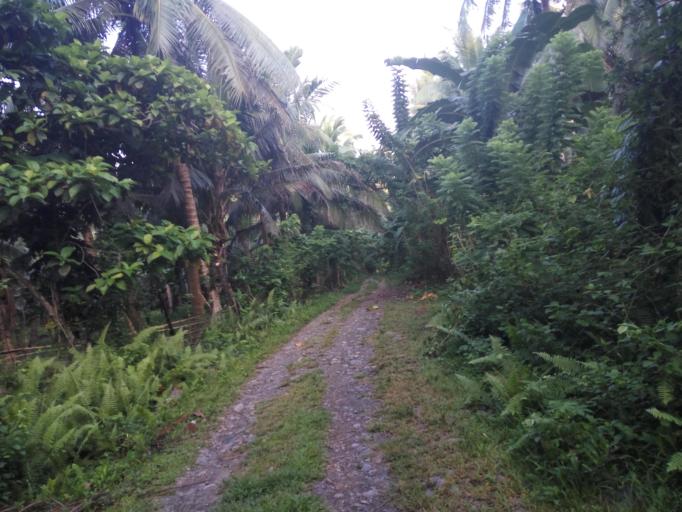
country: PH
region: Central Luzon
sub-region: Province of Aurora
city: Maria Aurora
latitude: 15.8890
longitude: 121.5466
